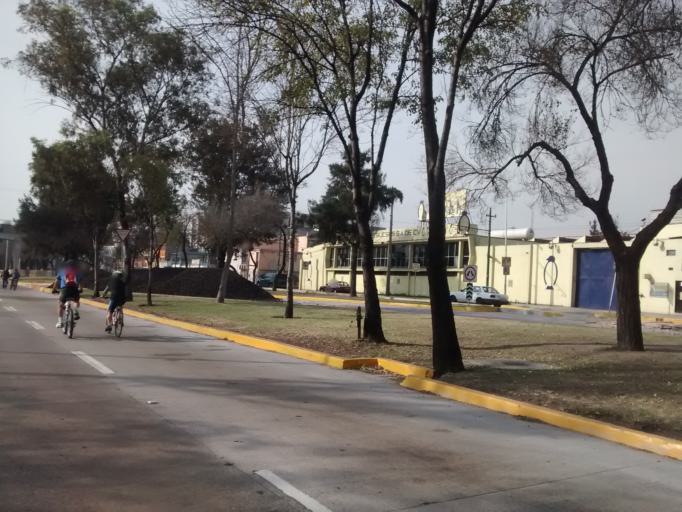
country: MX
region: Mexico City
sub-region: Iztacalco
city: Iztacalco
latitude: 19.3995
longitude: -99.0985
